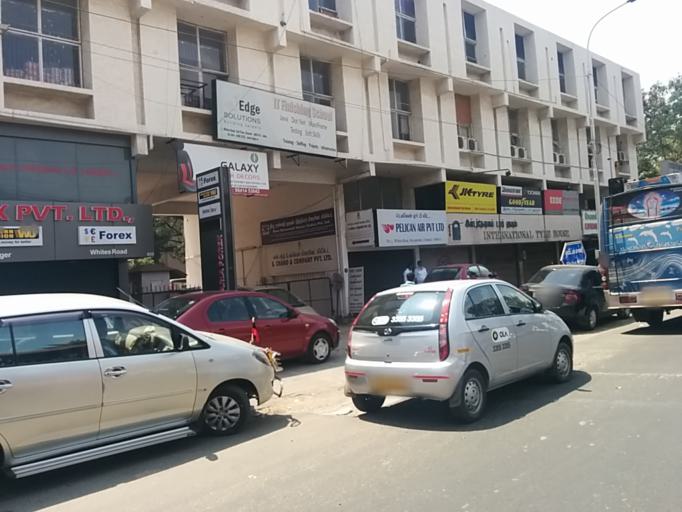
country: IN
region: Tamil Nadu
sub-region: Chennai
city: Chetput
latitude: 13.0579
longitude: 80.2630
